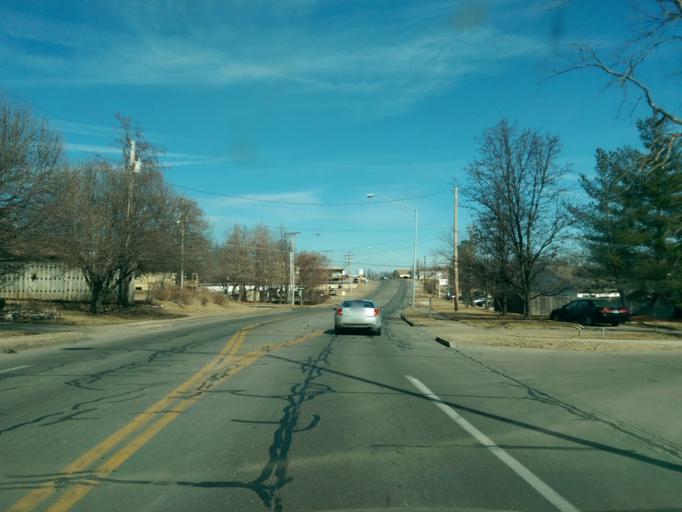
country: US
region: Missouri
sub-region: Boone County
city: Columbia
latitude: 38.9589
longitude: -92.3117
